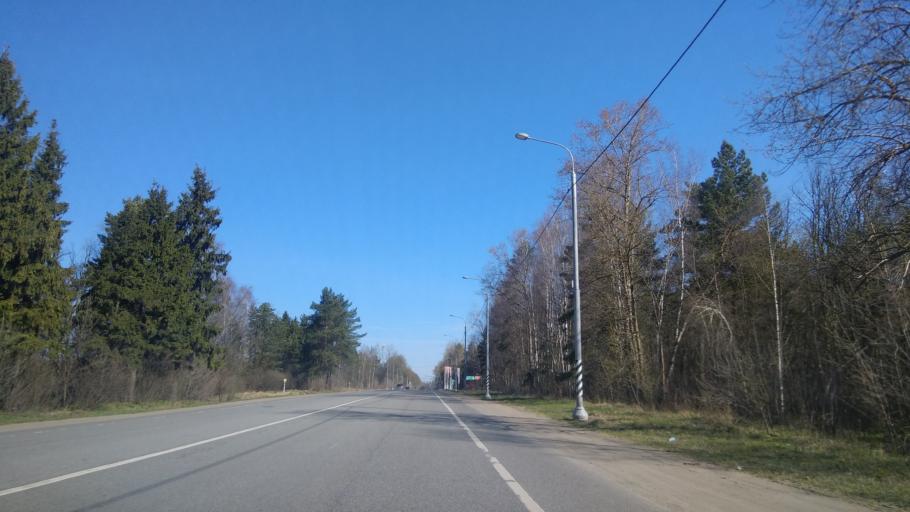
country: RU
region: Moskovskaya
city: Pushkino
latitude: 56.0281
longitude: 37.8711
